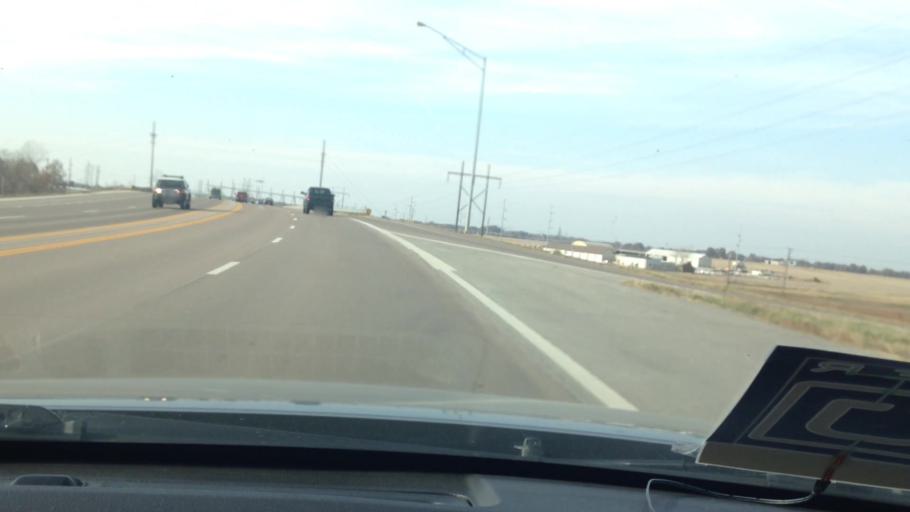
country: US
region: Missouri
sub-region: Henry County
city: Clinton
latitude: 38.3848
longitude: -93.7535
